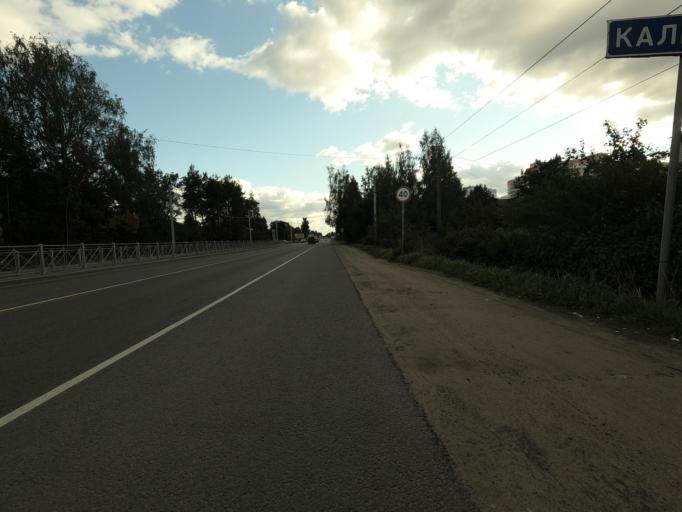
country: RU
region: Leningrad
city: Vsevolozhsk
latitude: 59.9903
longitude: 30.6576
